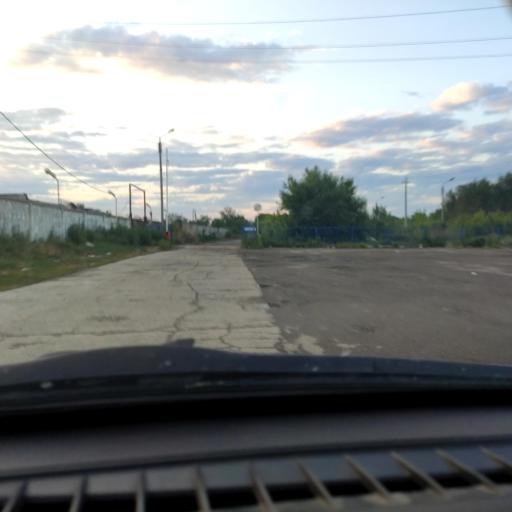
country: RU
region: Samara
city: Tol'yatti
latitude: 53.5692
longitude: 49.4668
